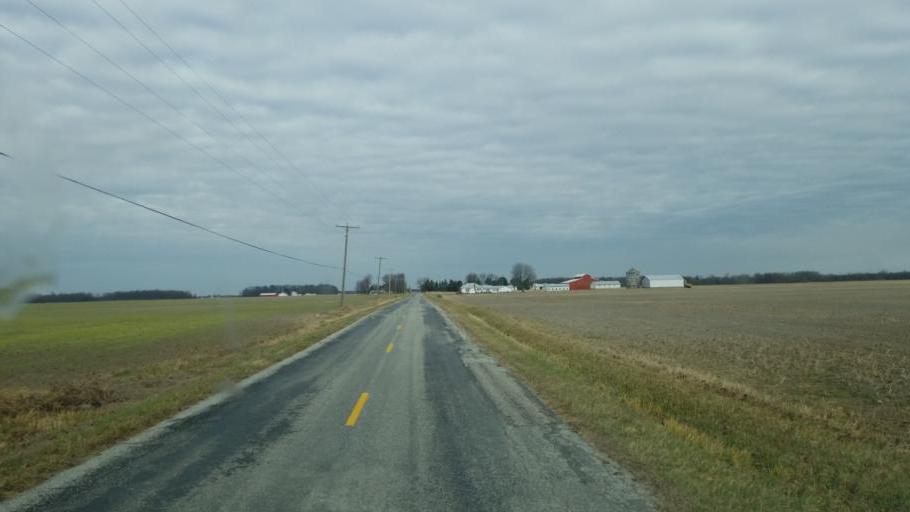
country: US
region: Ohio
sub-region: Hardin County
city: Forest
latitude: 40.6560
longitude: -83.4196
